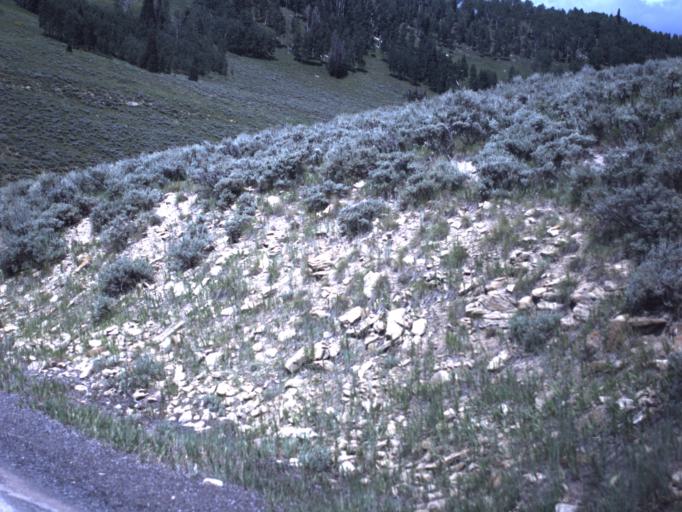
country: US
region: Utah
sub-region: Sanpete County
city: Fairview
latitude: 39.6873
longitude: -111.2453
